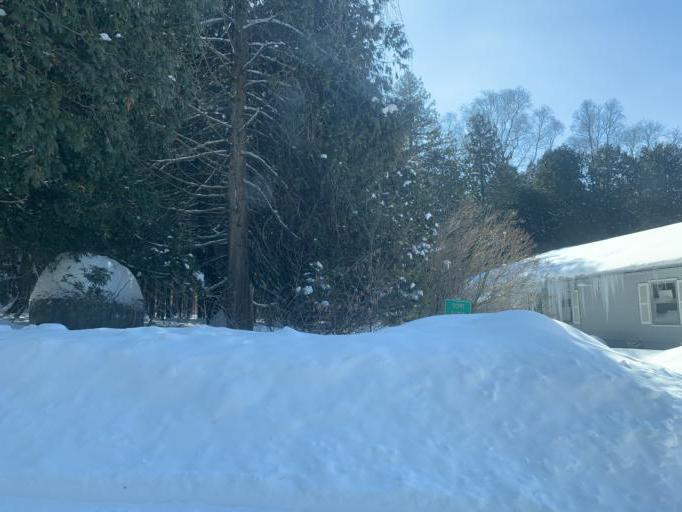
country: US
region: Wisconsin
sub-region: Door County
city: Sturgeon Bay
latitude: 45.1123
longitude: -87.2590
